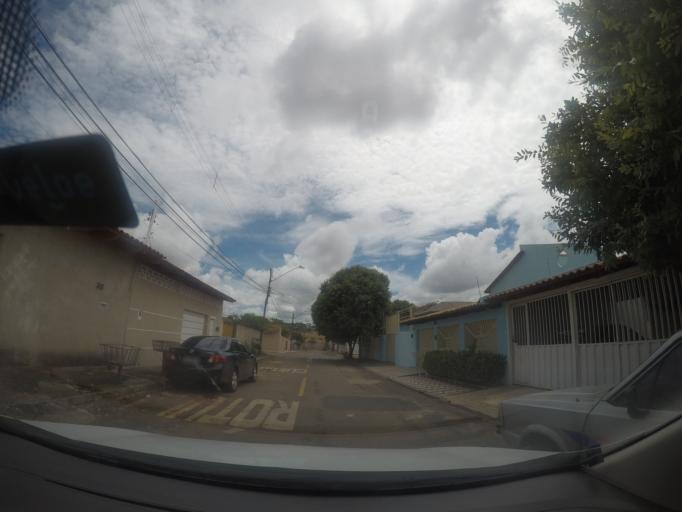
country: BR
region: Goias
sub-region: Goiania
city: Goiania
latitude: -16.6586
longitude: -49.2982
